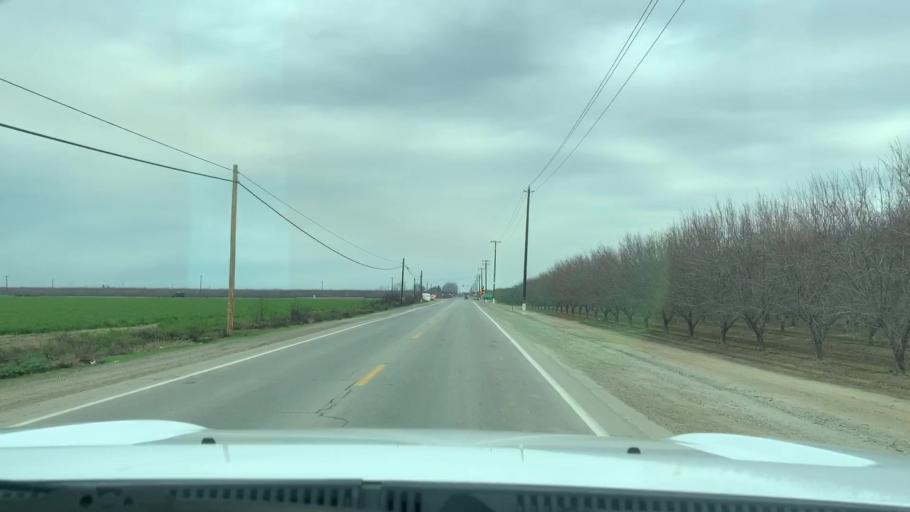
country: US
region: California
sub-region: Kern County
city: Rosedale
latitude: 35.3945
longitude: -119.2520
